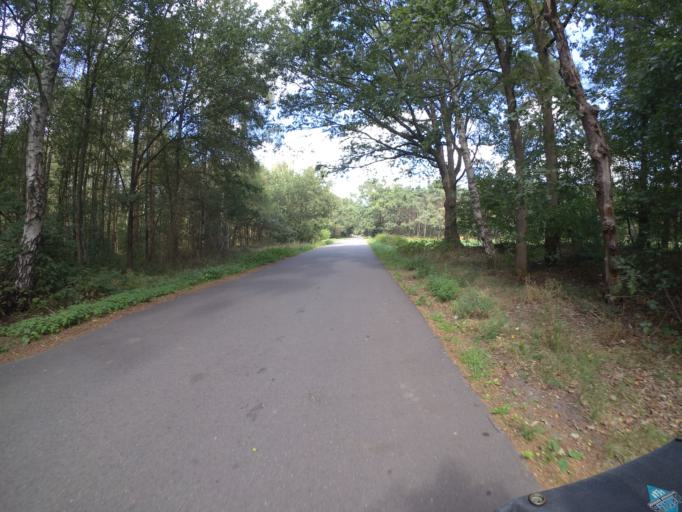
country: NL
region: North Brabant
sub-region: Gemeente Veghel
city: Eerde
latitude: 51.6005
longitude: 5.4887
